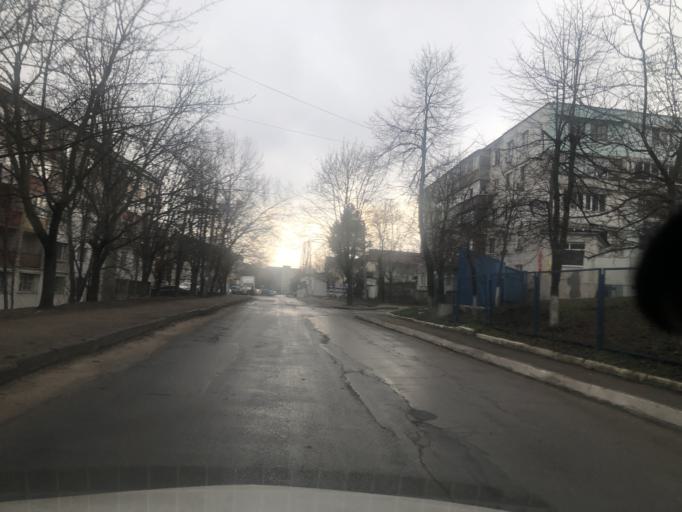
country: MD
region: Chisinau
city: Stauceni
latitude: 47.0654
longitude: 28.8396
